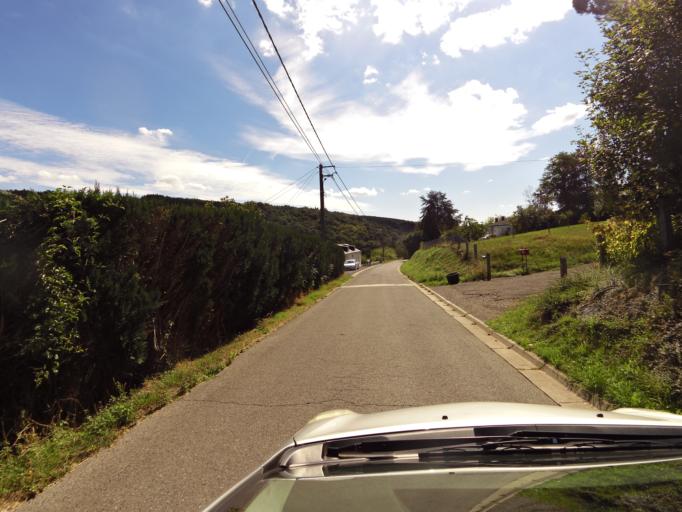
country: BE
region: Wallonia
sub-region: Province du Luxembourg
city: Rendeux
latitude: 50.2264
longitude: 5.5226
